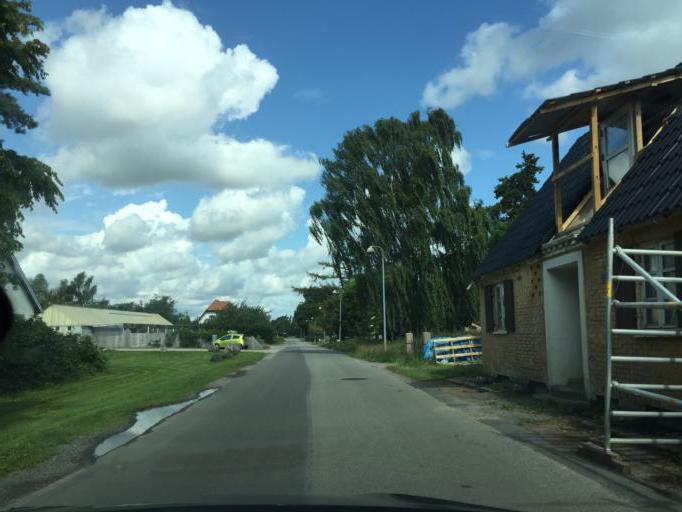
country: DK
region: South Denmark
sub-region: Odense Kommune
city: Stige
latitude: 55.4430
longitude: 10.3910
